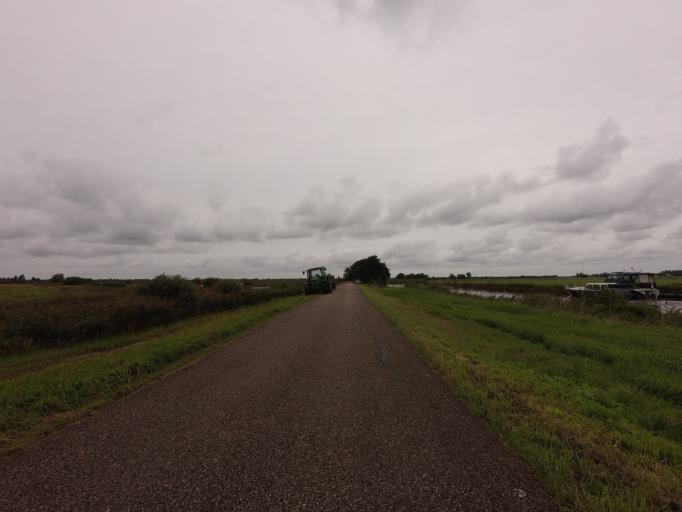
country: NL
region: Overijssel
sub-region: Gemeente Steenwijkerland
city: Oldemarkt
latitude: 52.8254
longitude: 5.9230
